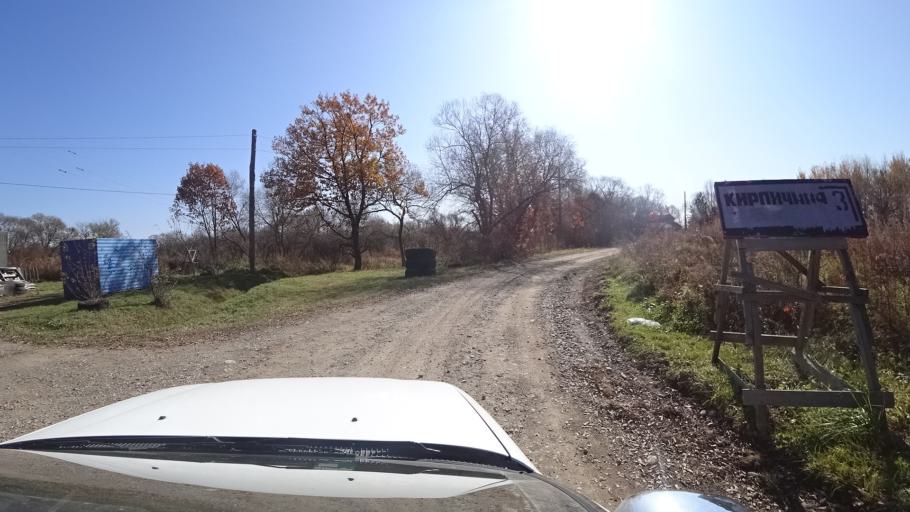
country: RU
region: Primorskiy
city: Dal'nerechensk
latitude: 45.9210
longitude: 133.7839
